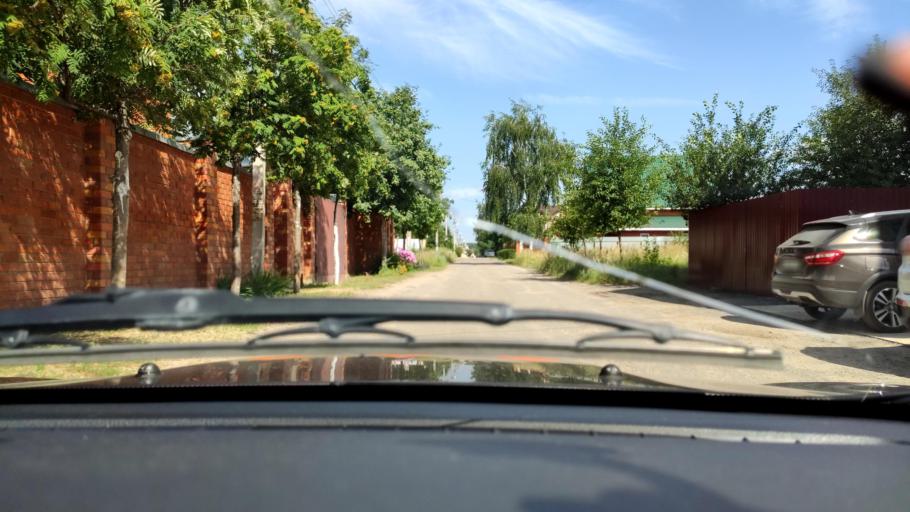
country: RU
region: Voronezj
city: Podgornoye
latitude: 51.7439
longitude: 39.1468
